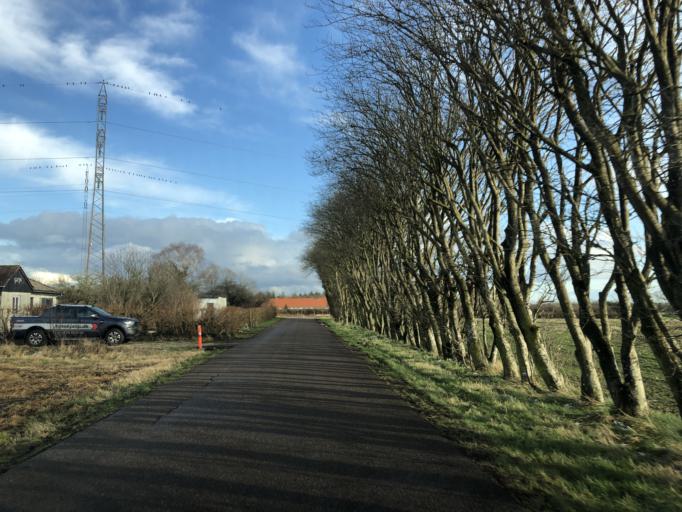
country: DK
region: Central Jutland
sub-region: Viborg Kommune
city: Viborg
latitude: 56.5023
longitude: 9.4334
